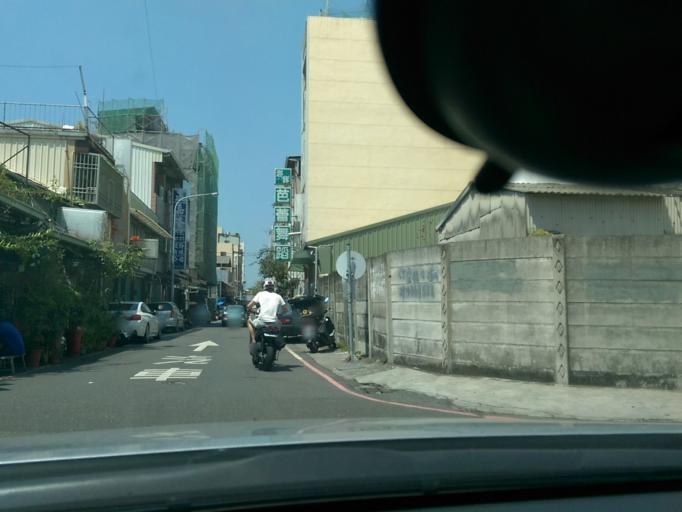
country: TW
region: Taiwan
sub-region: Chiayi
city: Jiayi Shi
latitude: 23.4824
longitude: 120.4502
